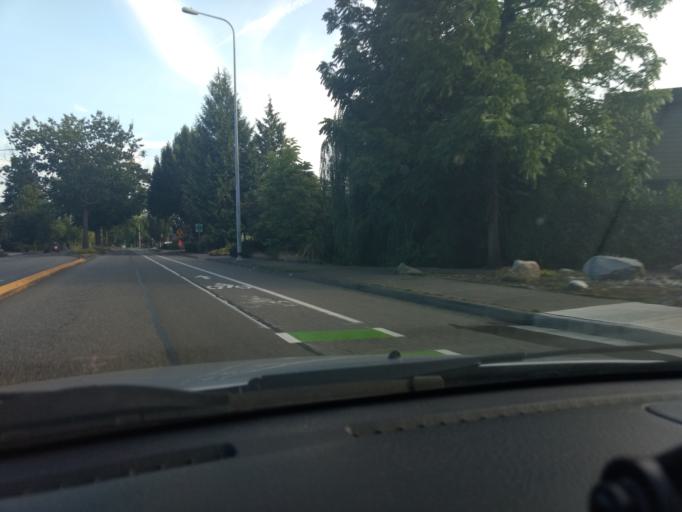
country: US
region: Washington
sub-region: King County
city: Kirkland
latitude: 47.6854
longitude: -122.2098
